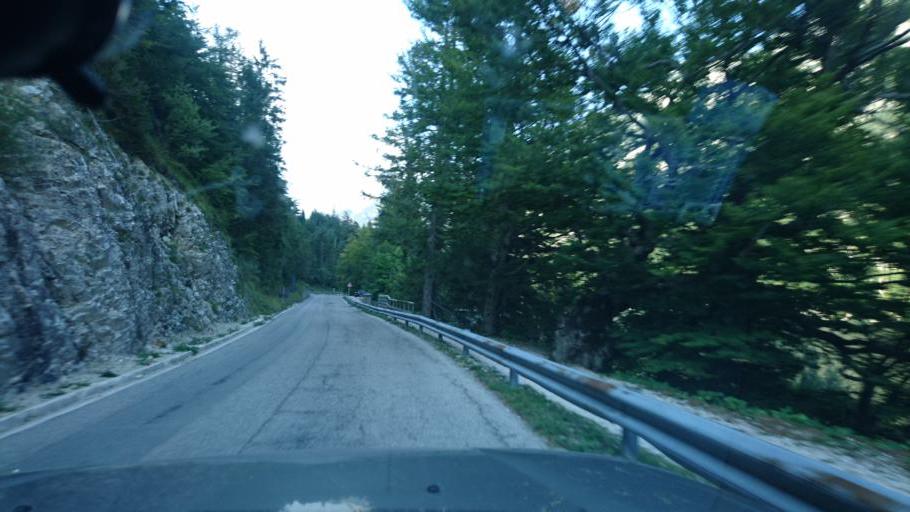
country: SI
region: Bovec
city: Bovec
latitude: 46.4219
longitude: 13.5628
